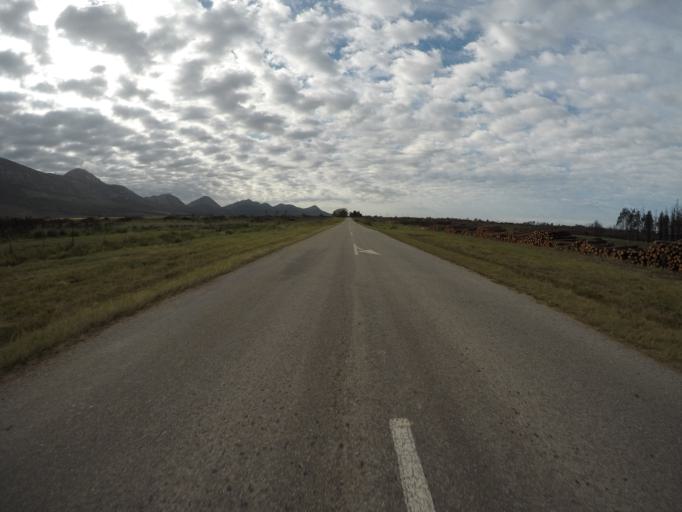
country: ZA
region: Eastern Cape
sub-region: Cacadu District Municipality
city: Kareedouw
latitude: -34.0429
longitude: 24.4201
